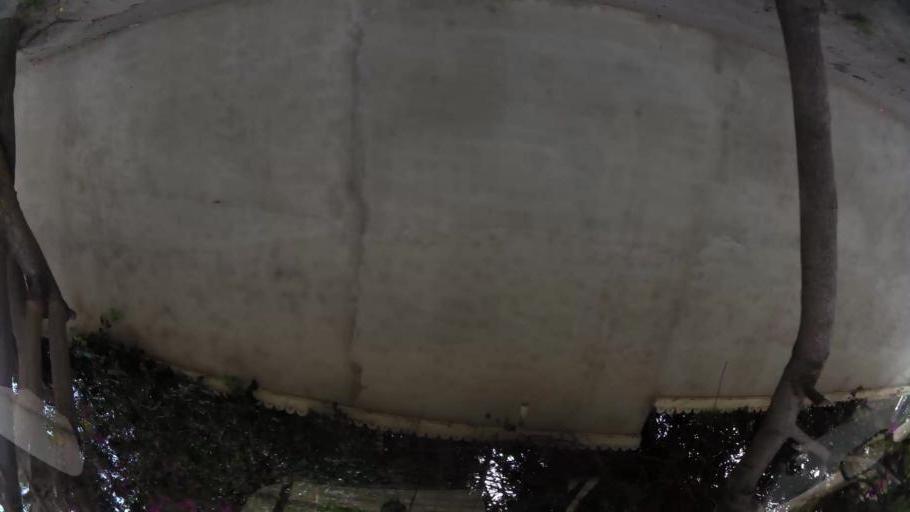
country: MA
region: Gharb-Chrarda-Beni Hssen
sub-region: Kenitra Province
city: Kenitra
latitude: 34.2644
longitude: -6.5944
